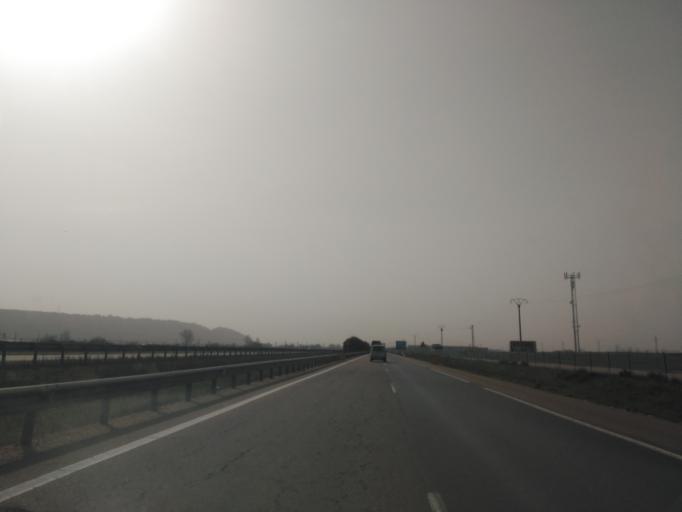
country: ES
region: Castille and Leon
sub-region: Provincia de Valladolid
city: Cabezon
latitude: 41.7659
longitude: -4.6268
